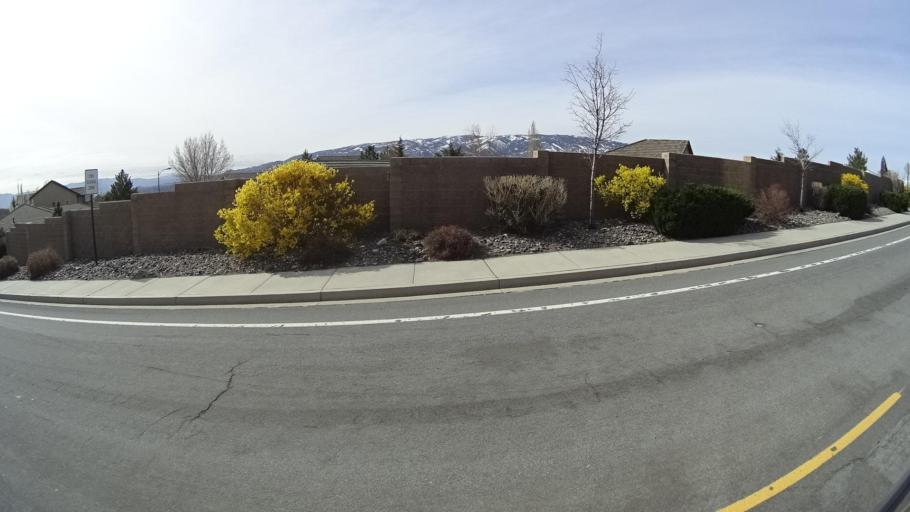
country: US
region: Nevada
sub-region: Washoe County
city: Mogul
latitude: 39.5469
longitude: -119.8912
